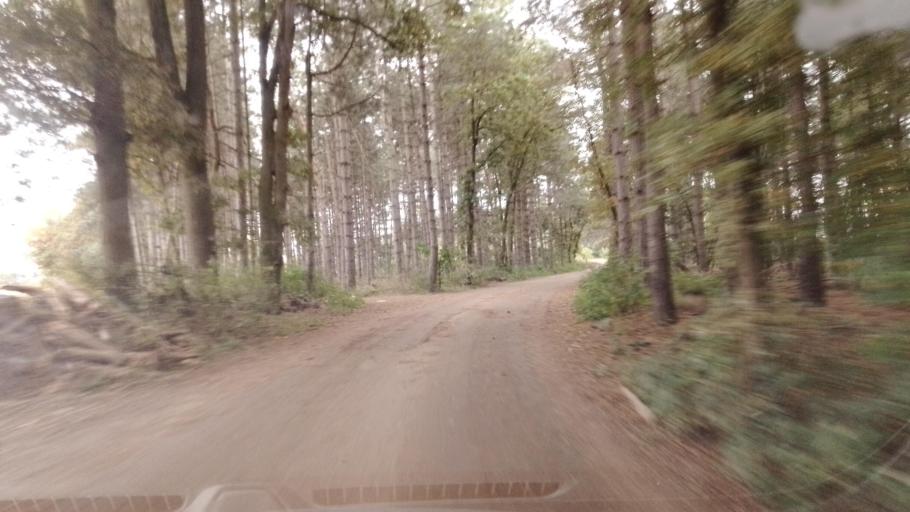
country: NL
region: Limburg
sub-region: Gemeente Venlo
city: Tegelen
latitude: 51.3916
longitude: 6.1162
